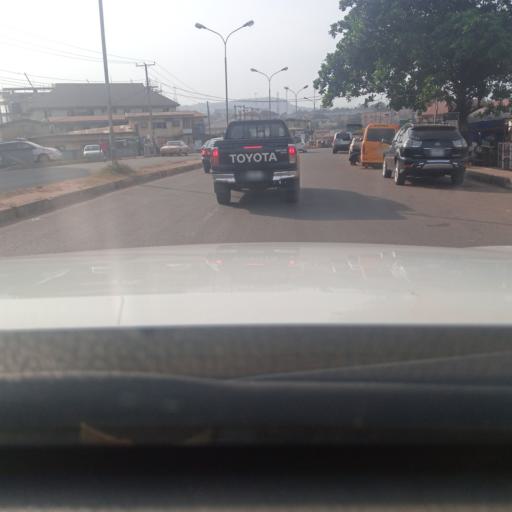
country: NG
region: Enugu
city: Enugu
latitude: 6.4407
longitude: 7.5036
